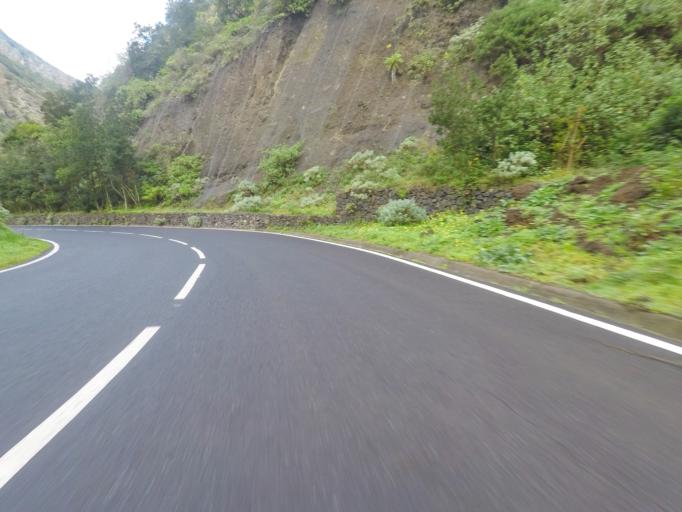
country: ES
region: Canary Islands
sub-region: Provincia de Santa Cruz de Tenerife
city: Hermigua
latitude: 28.1331
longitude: -17.1986
